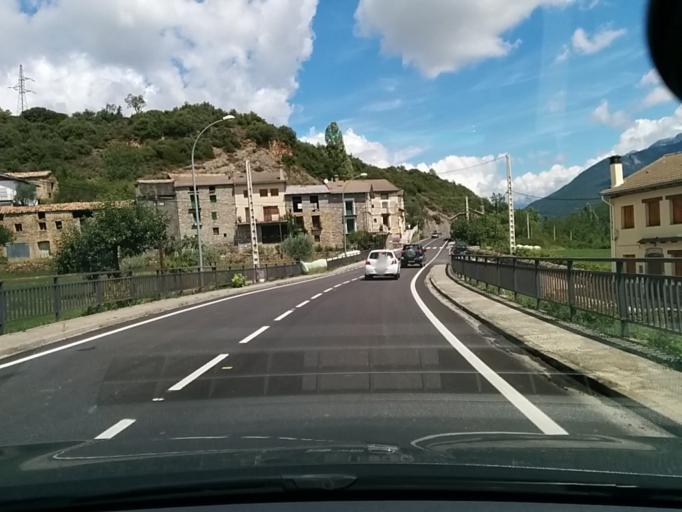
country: ES
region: Aragon
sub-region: Provincia de Huesca
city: Labuerda
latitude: 42.4517
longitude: 0.1341
